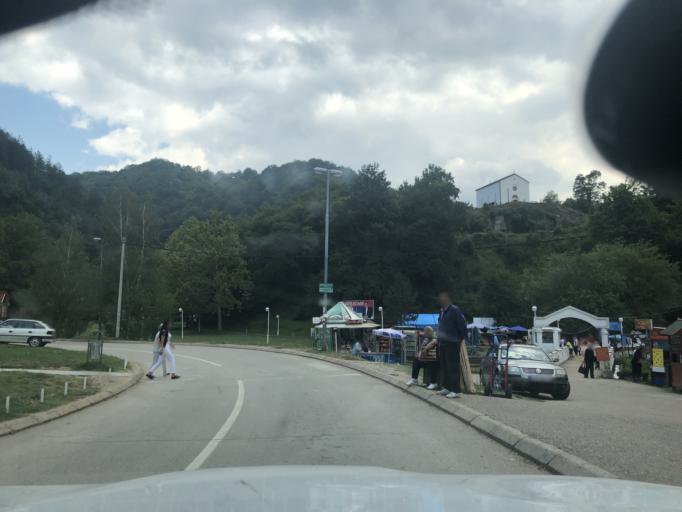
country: RS
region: Central Serbia
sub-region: Jablanicki Okrug
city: Medvega
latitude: 42.7767
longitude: 21.6021
